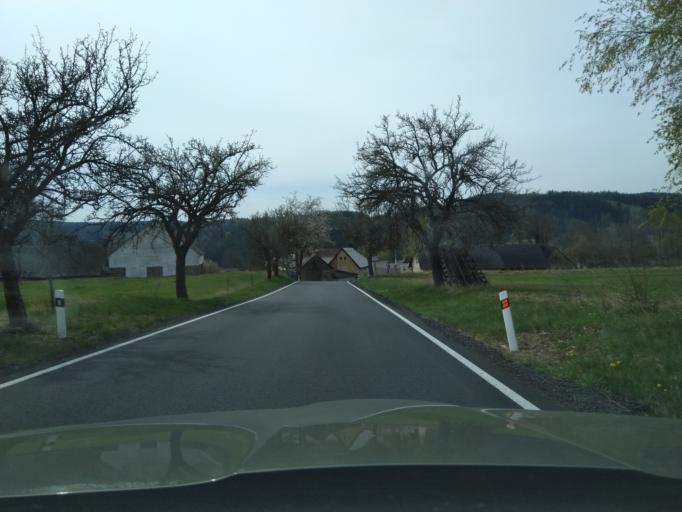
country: CZ
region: Jihocesky
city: Vacov
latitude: 49.1185
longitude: 13.7462
